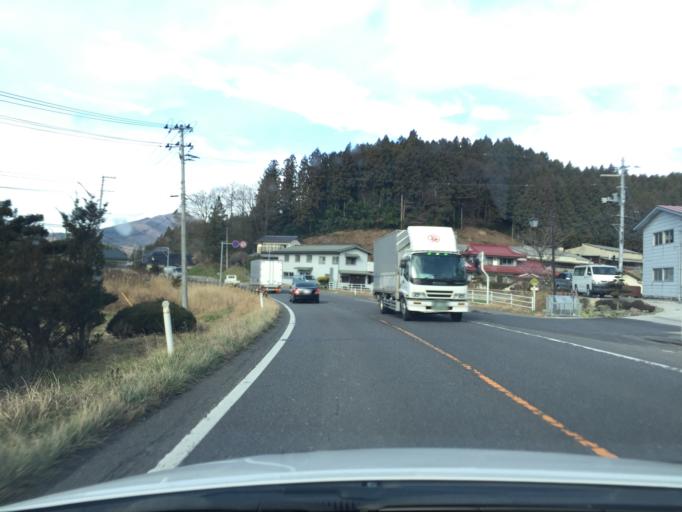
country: JP
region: Fukushima
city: Ishikawa
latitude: 37.2330
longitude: 140.5771
